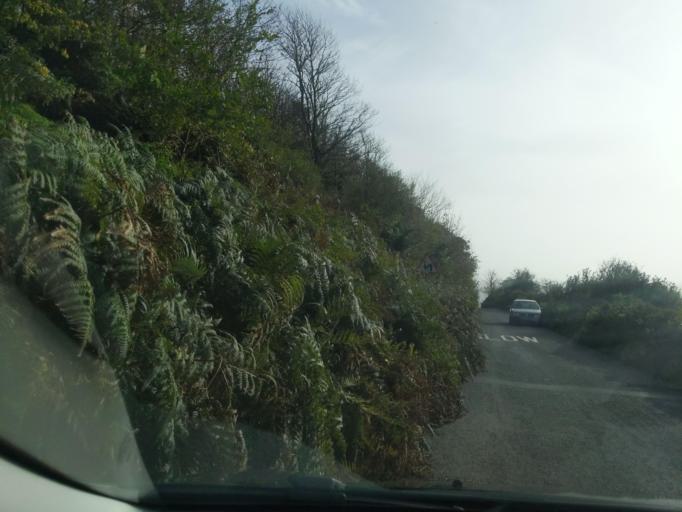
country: GB
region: England
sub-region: Cornwall
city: Looe
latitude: 50.3628
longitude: -4.3599
